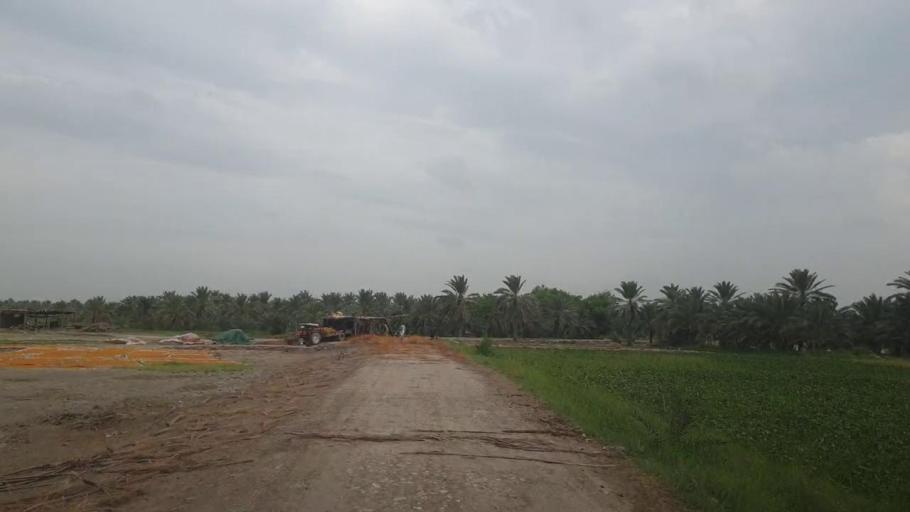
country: PK
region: Sindh
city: Khairpur
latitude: 27.5914
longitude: 68.7404
